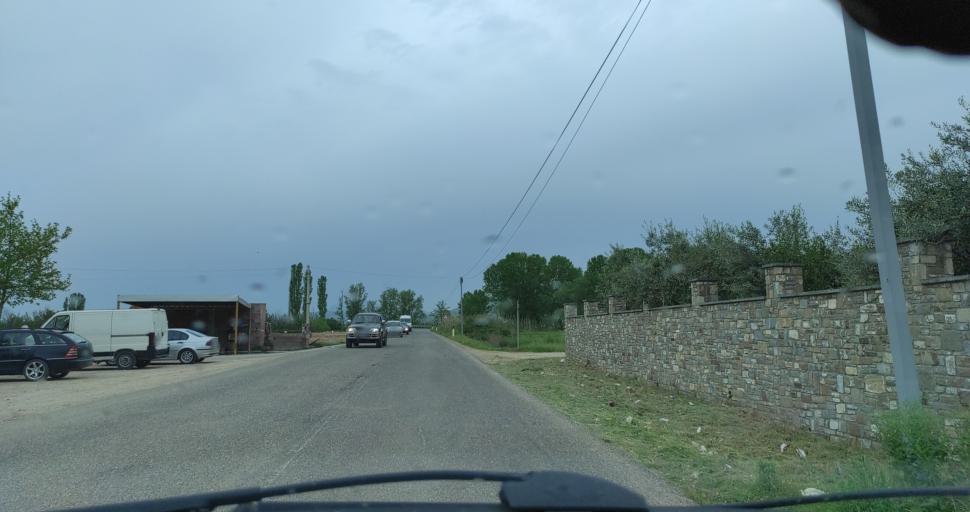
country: AL
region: Lezhe
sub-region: Rrethi i Kurbinit
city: Mamurras
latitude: 41.5985
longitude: 19.6994
